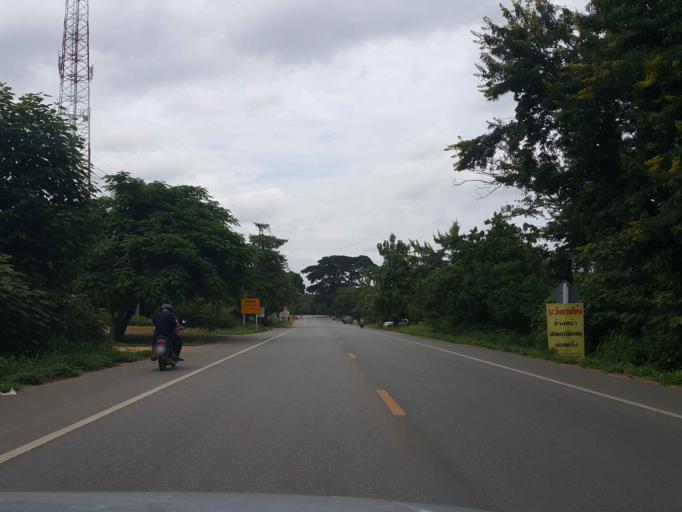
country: TH
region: Lamphun
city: Li
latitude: 17.7918
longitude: 98.9529
